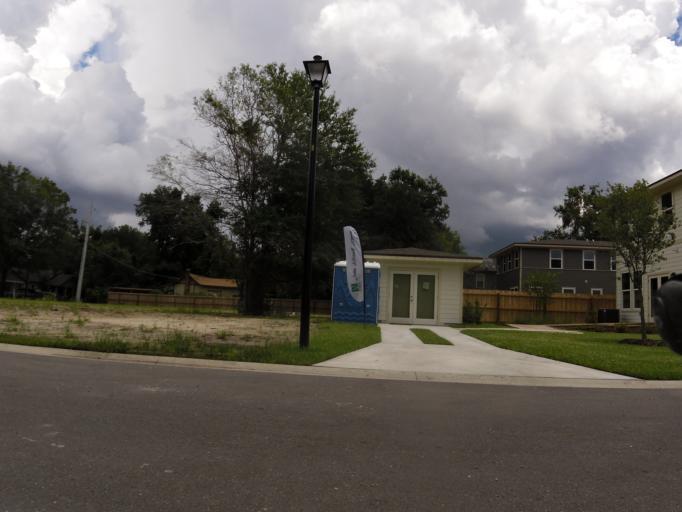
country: US
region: Florida
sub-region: Duval County
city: Jacksonville
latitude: 30.3155
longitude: -81.7002
